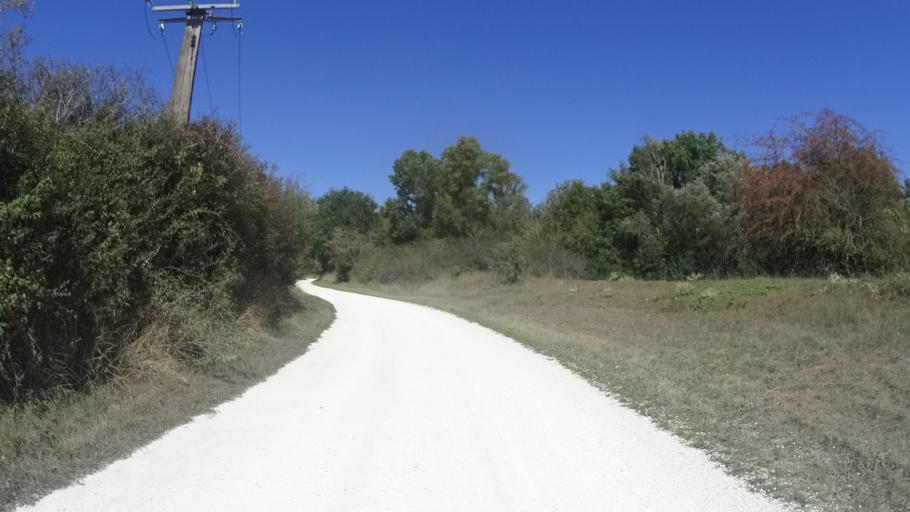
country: FR
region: Centre
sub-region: Departement du Loiret
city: Bonny-sur-Loire
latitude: 47.5367
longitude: 2.8443
